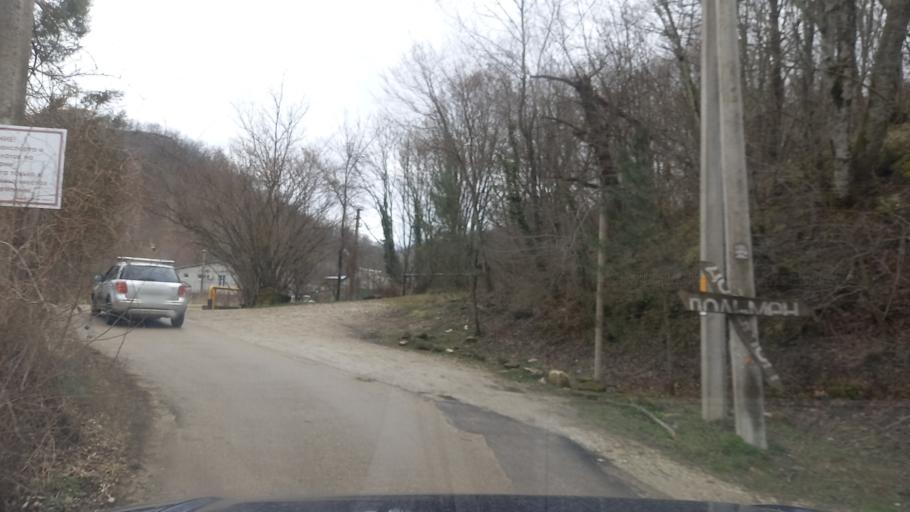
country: RU
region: Krasnodarskiy
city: Pshada
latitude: 44.4806
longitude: 38.4067
